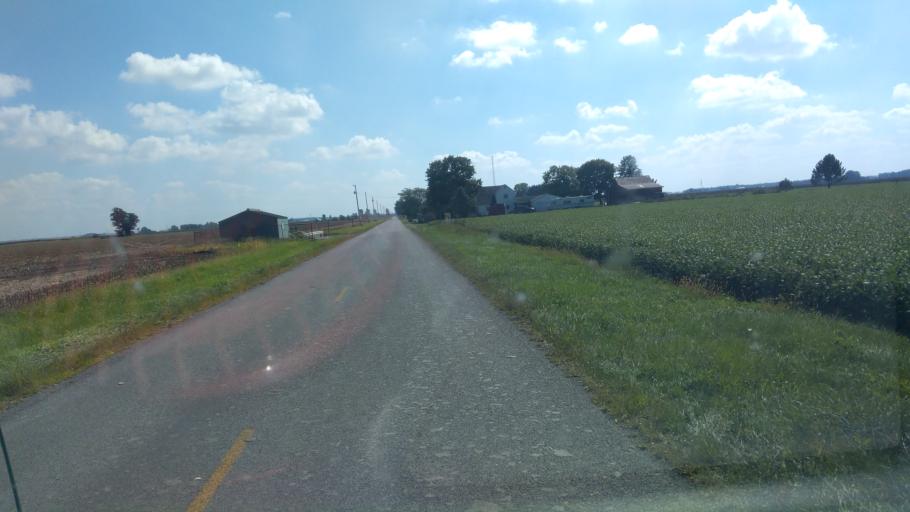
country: US
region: Ohio
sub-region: Hardin County
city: Ada
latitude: 40.6976
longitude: -83.8421
